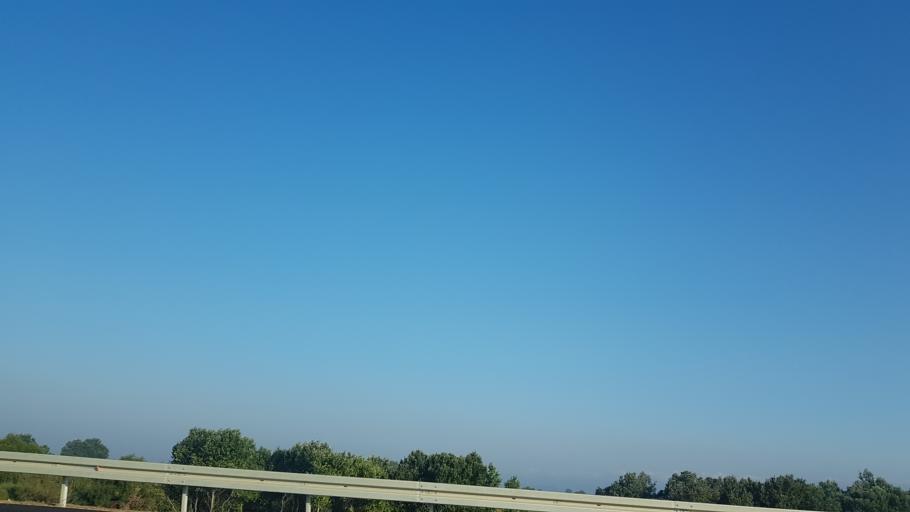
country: TR
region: Bursa
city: Karacabey
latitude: 40.1835
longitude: 28.3323
